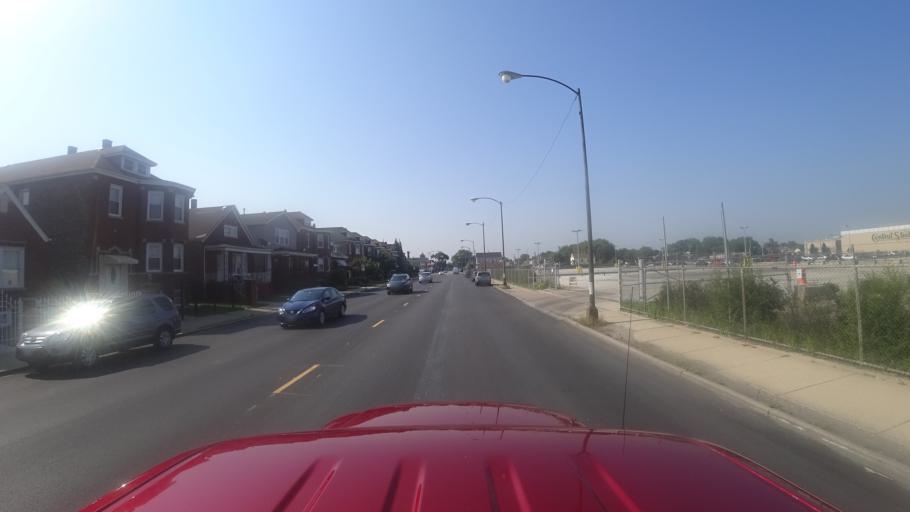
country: US
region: Illinois
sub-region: Cook County
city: Chicago
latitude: 41.8027
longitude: -87.6941
